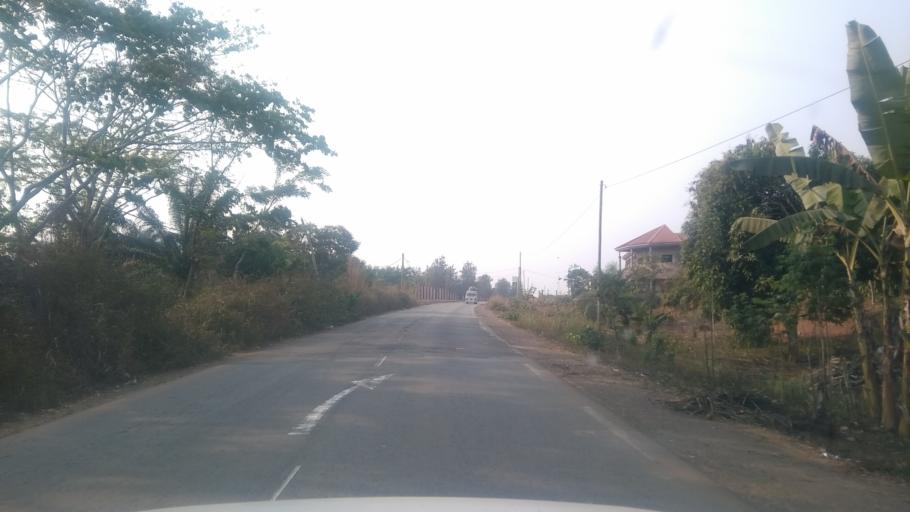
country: CM
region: West
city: Tonga
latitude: 4.9708
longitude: 10.7089
